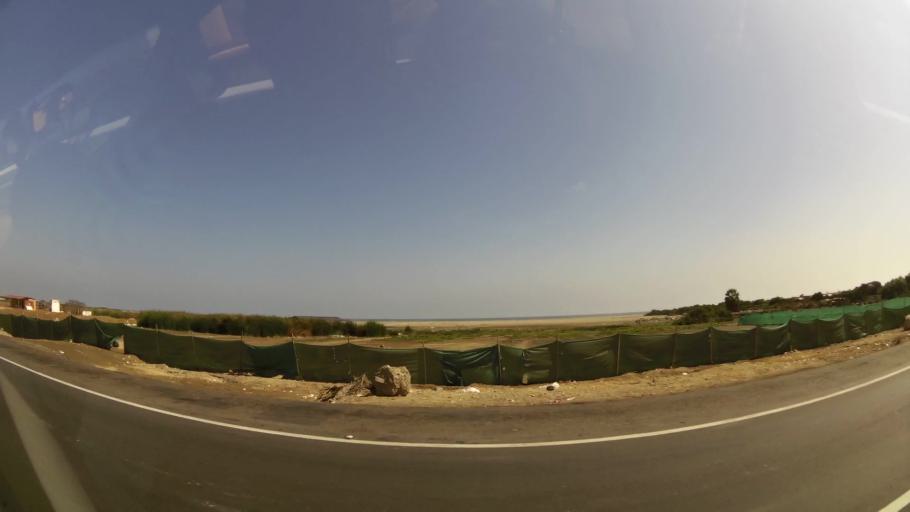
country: PE
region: Ica
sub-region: Provincia de Chincha
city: San Pedro
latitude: -13.3852
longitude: -76.2032
